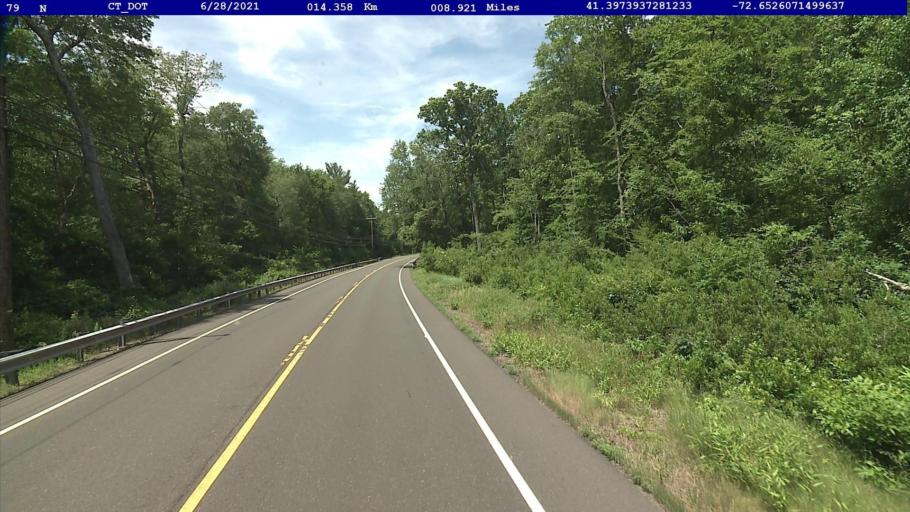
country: US
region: Connecticut
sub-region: Middlesex County
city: Durham
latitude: 41.3974
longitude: -72.6526
